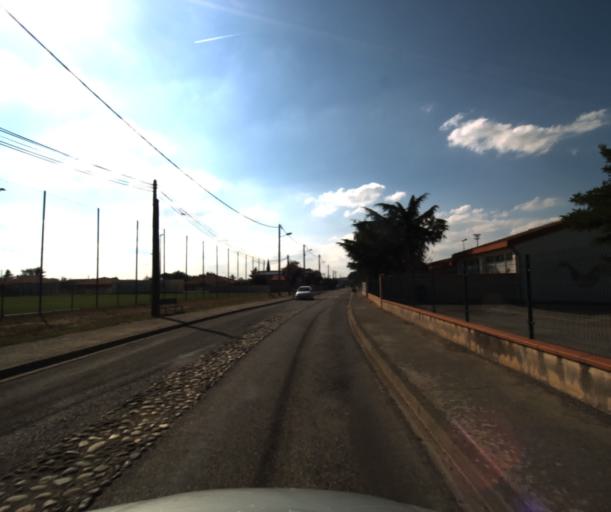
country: FR
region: Midi-Pyrenees
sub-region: Departement de la Haute-Garonne
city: Saint-Lys
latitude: 43.5105
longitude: 1.1833
